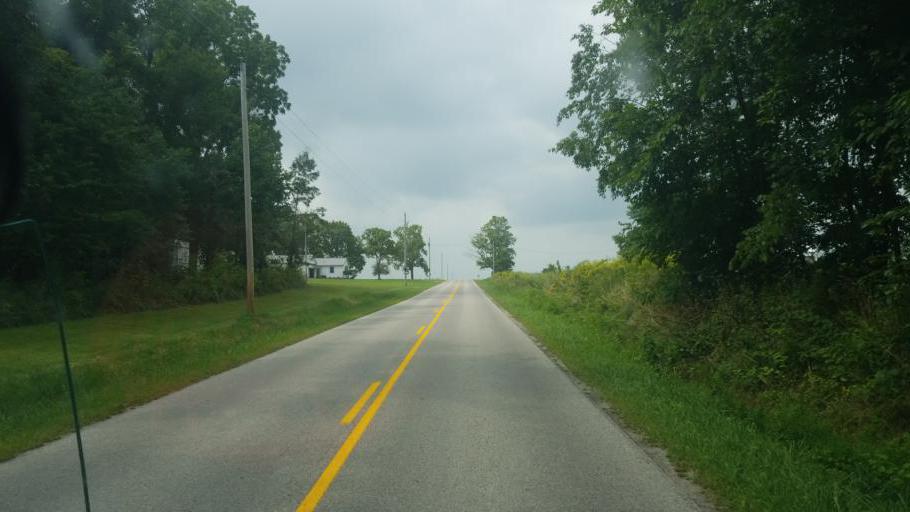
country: US
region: Ohio
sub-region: Huron County
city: Greenwich
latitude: 41.0873
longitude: -82.5707
